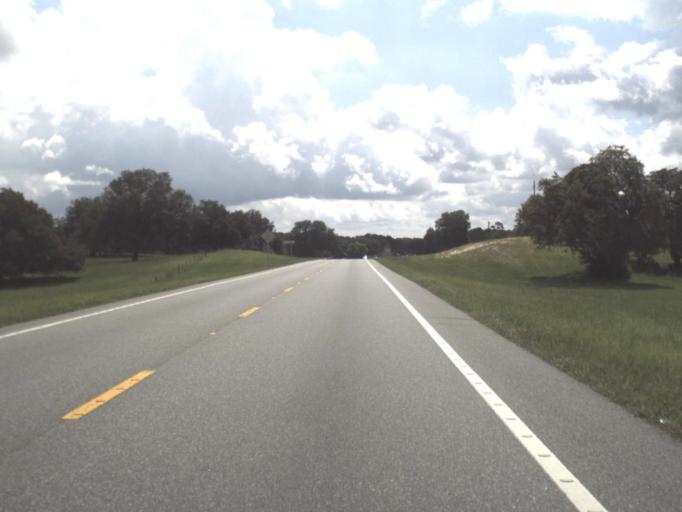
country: US
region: Florida
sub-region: Hernando County
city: Ridge Manor
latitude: 28.5078
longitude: -82.1661
